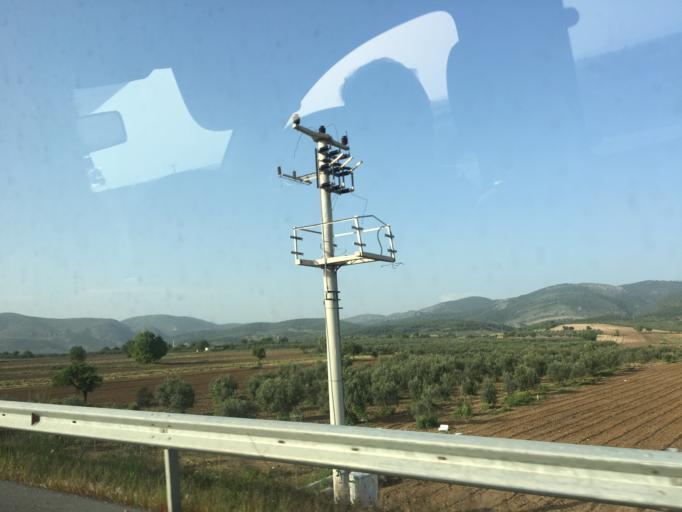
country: TR
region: Manisa
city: Golmarmara
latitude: 38.7943
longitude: 27.8982
